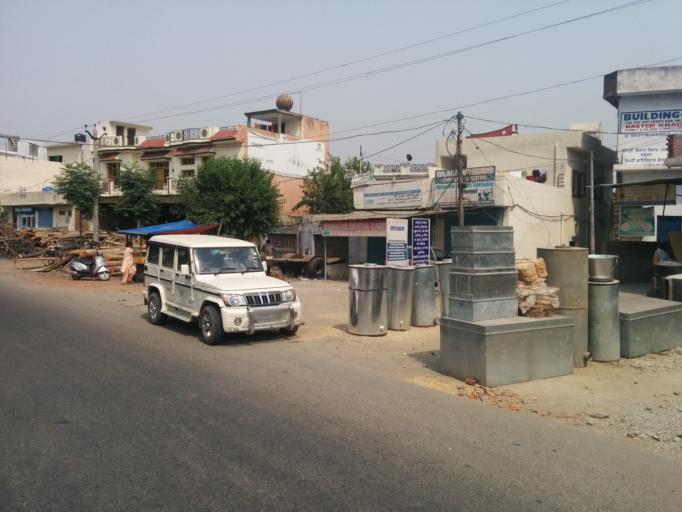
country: IN
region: Punjab
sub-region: Pathankot
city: Pathankot
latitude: 32.2626
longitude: 75.5908
